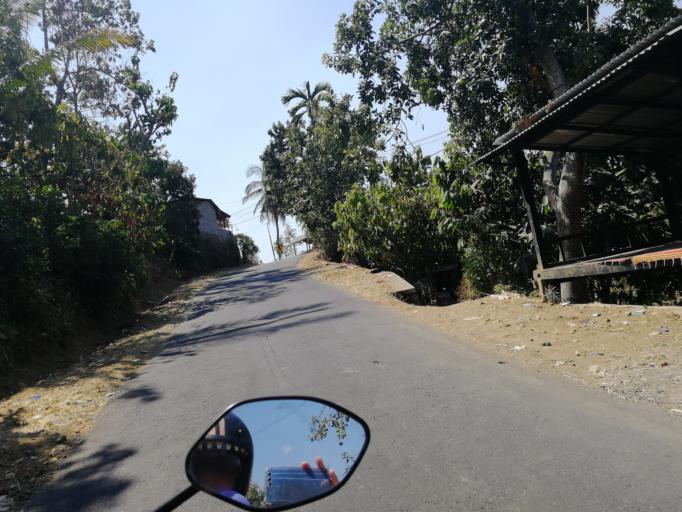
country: ID
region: Bali
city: Banjar Kedisan
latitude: -8.1431
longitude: 115.3124
